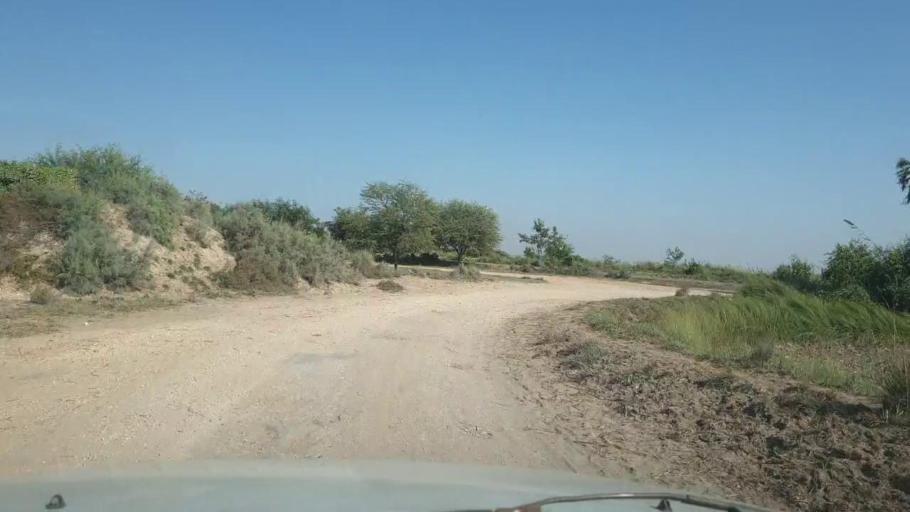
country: PK
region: Sindh
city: Chuhar Jamali
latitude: 24.4845
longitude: 67.8199
